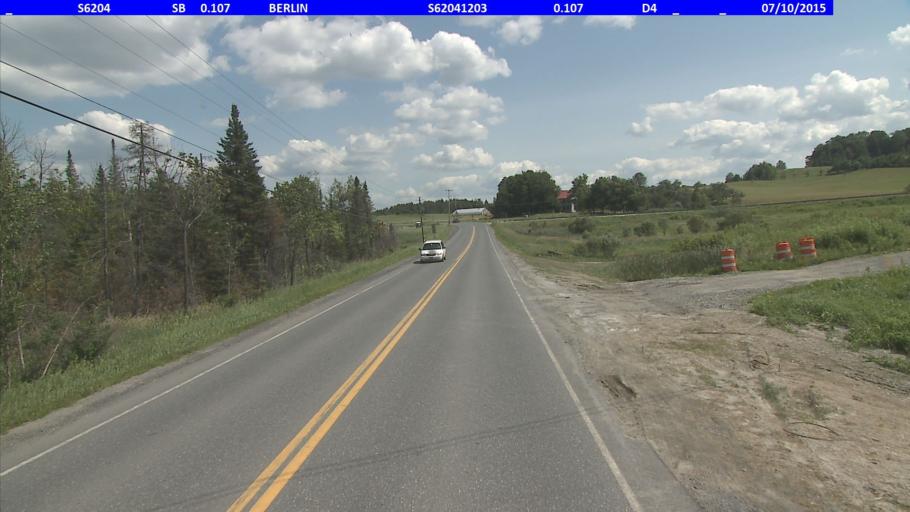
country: US
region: Vermont
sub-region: Washington County
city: South Barre
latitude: 44.1944
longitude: -72.5567
